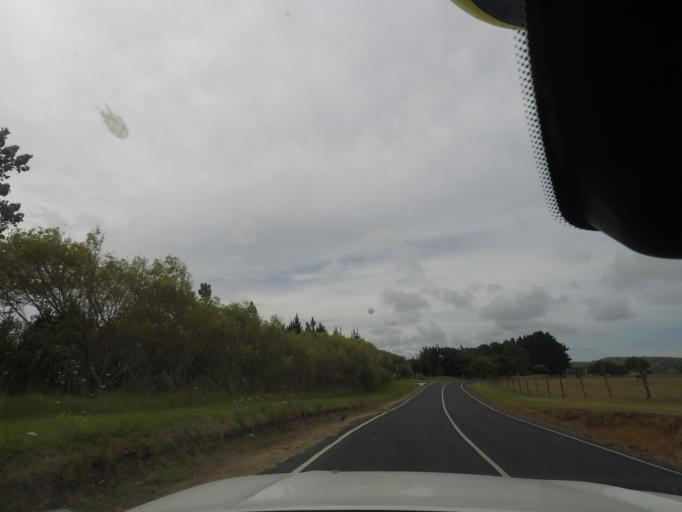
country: NZ
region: Auckland
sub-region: Auckland
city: Parakai
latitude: -36.5135
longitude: 174.2481
